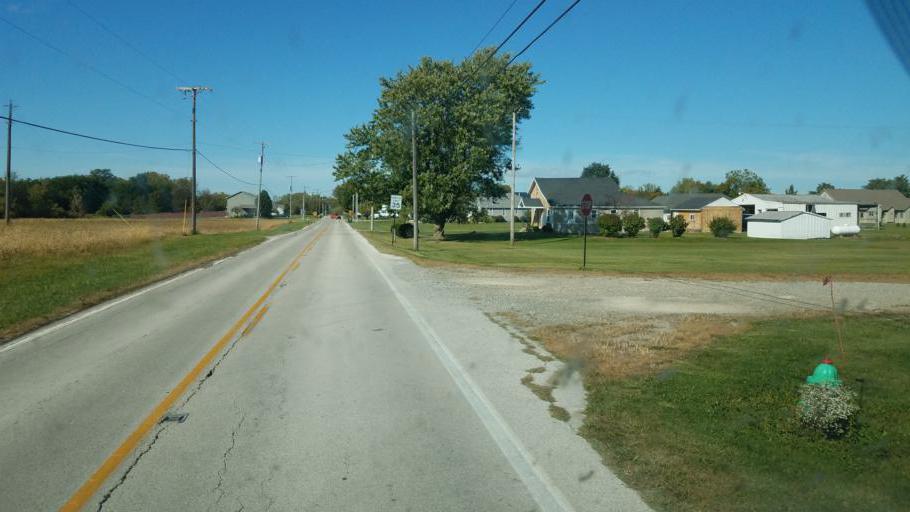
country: US
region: Ohio
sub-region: Wyandot County
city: Upper Sandusky
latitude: 40.8255
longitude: -83.2627
